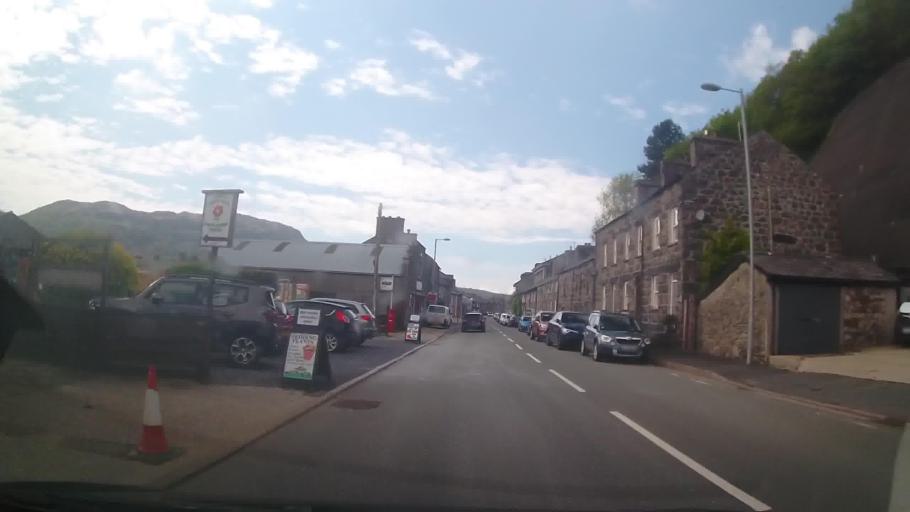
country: GB
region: Wales
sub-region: Gwynedd
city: Porthmadog
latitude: 52.9407
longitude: -4.1396
